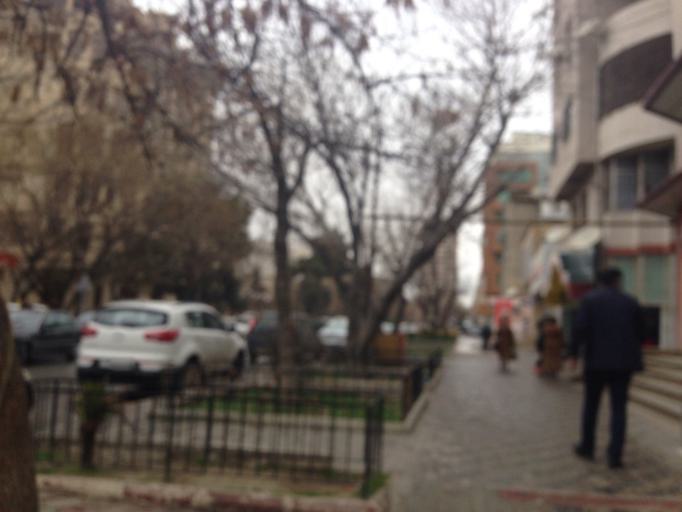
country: AZ
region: Baki
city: Baku
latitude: 40.4070
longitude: 49.8689
